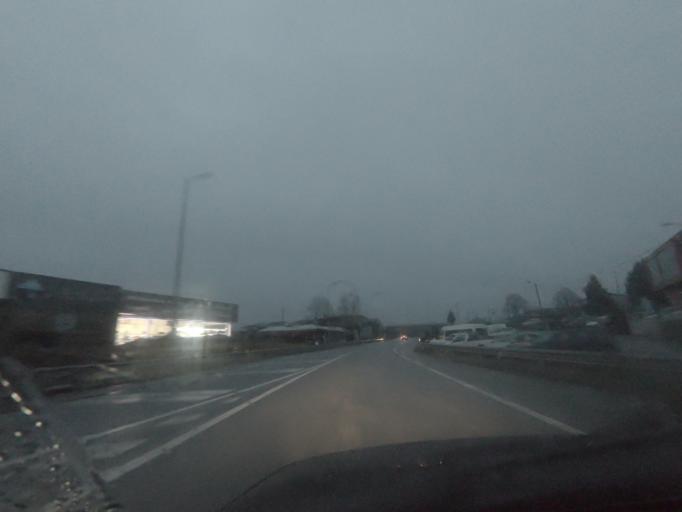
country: PT
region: Vila Real
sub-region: Vila Real
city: Vila Real
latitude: 41.2812
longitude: -7.7046
